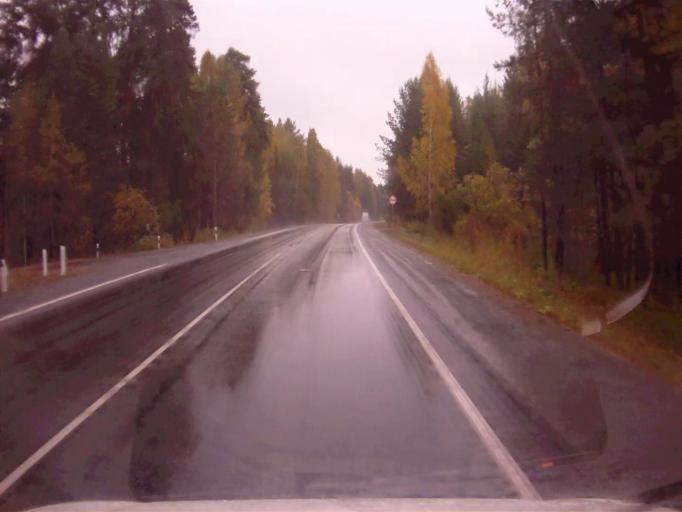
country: RU
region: Chelyabinsk
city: Tayginka
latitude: 55.5569
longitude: 60.6462
